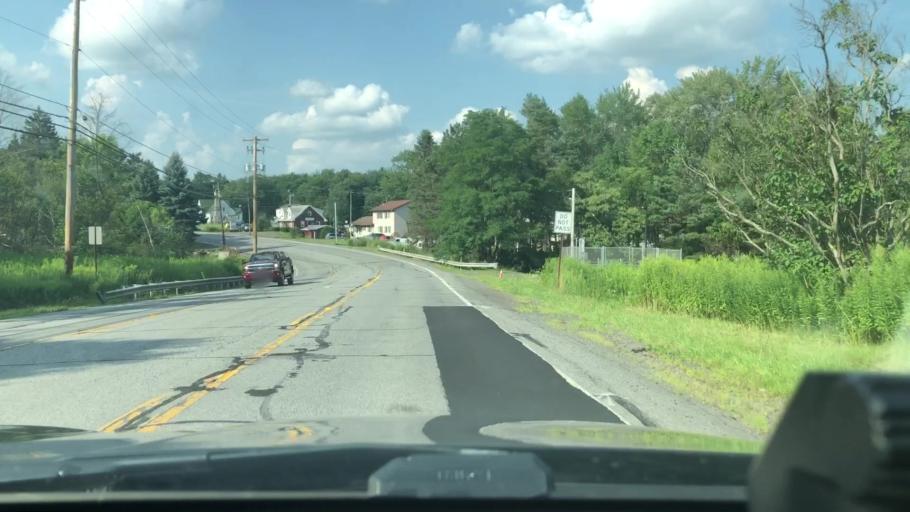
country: US
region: Pennsylvania
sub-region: Lackawanna County
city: Moscow
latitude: 41.2911
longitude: -75.5083
